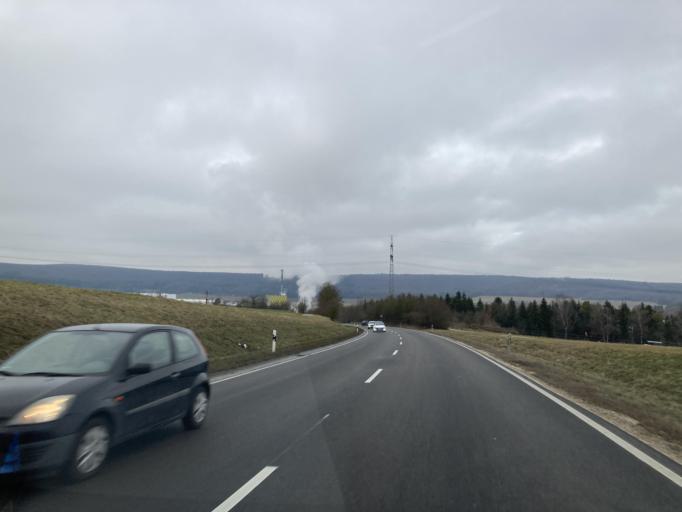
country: DE
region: Baden-Wuerttemberg
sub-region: Regierungsbezirk Stuttgart
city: Herbrechtingen
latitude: 48.6225
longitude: 10.2036
